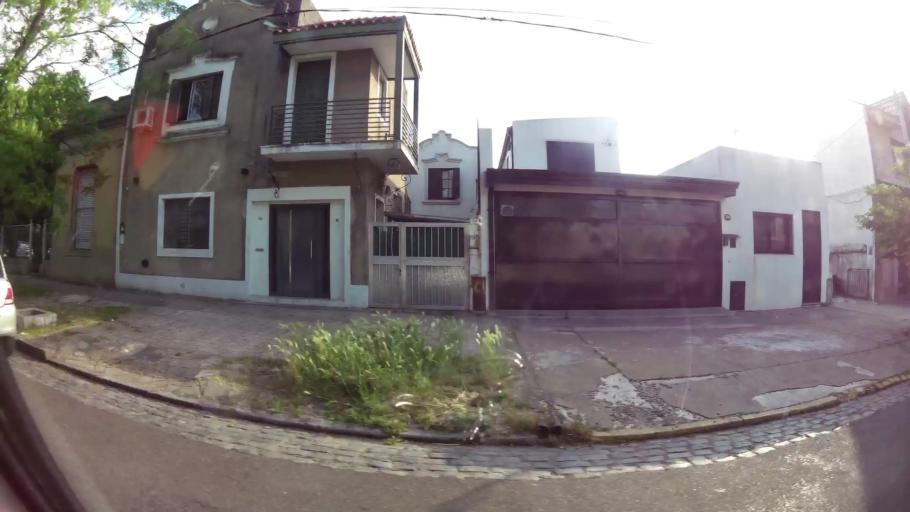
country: AR
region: Buenos Aires
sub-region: Partido de La Plata
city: La Plata
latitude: -34.8972
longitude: -57.9574
